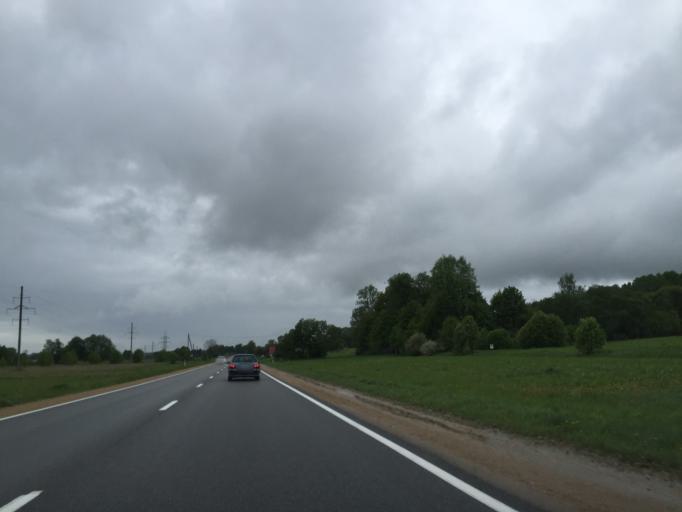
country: LV
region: Kegums
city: Kegums
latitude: 56.7616
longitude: 24.6907
